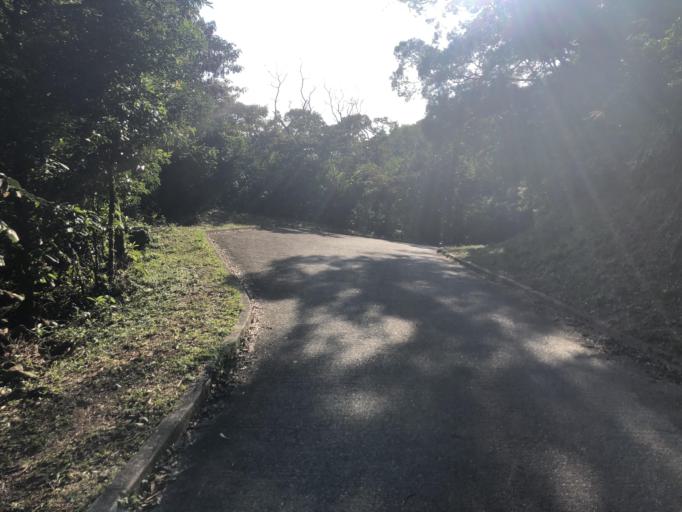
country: HK
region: Tsuen Wan
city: Tsuen Wan
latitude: 22.4007
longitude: 114.0841
